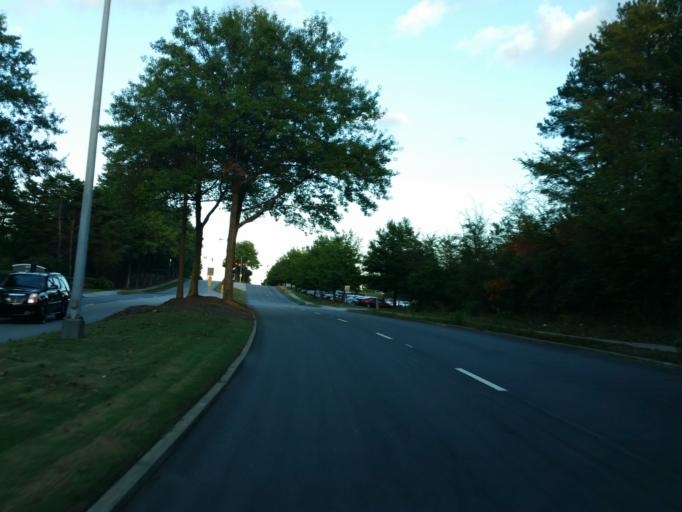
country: US
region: Georgia
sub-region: Cobb County
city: Vinings
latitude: 33.8273
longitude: -84.4978
